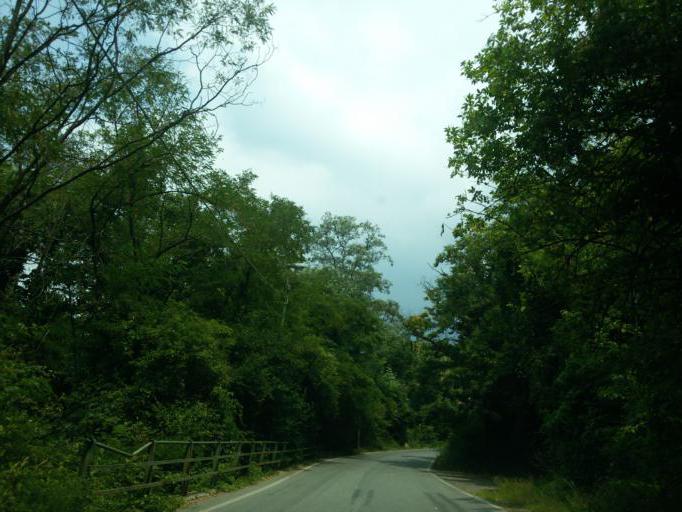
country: IT
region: Liguria
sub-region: Provincia di Genova
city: Piccarello
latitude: 44.4420
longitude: 8.9980
